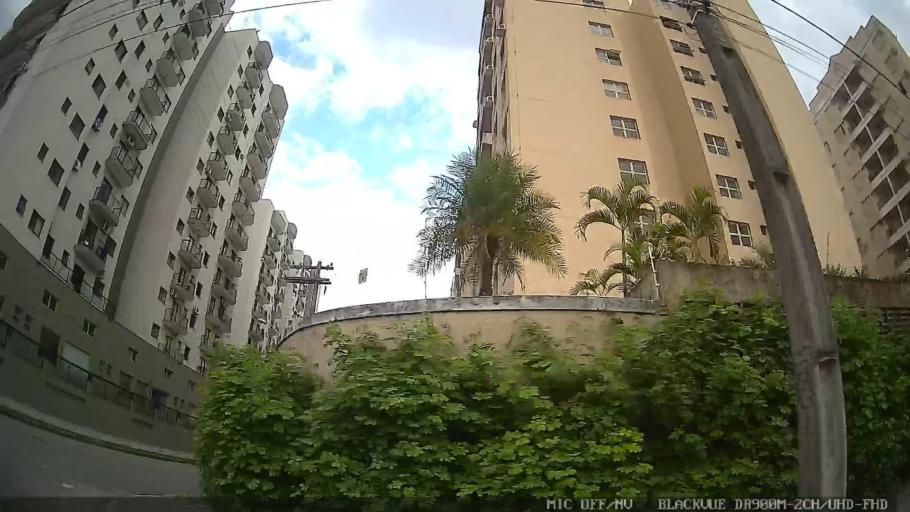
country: BR
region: Sao Paulo
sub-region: Guaruja
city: Guaruja
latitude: -23.9839
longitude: -46.2411
